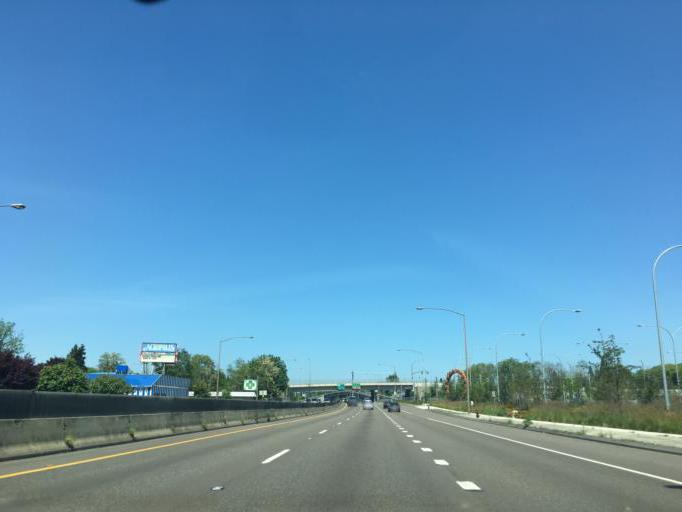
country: US
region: Oregon
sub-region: Clackamas County
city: Milwaukie
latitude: 45.4617
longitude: -122.6388
